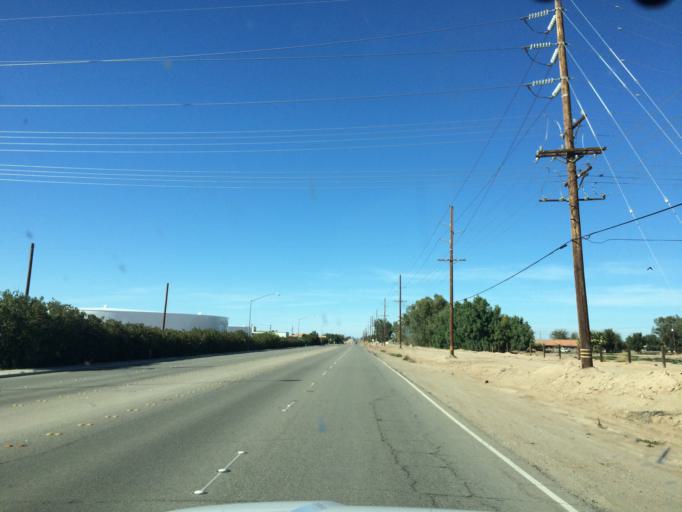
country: US
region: California
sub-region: Imperial County
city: El Centro
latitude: 32.7630
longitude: -115.5609
